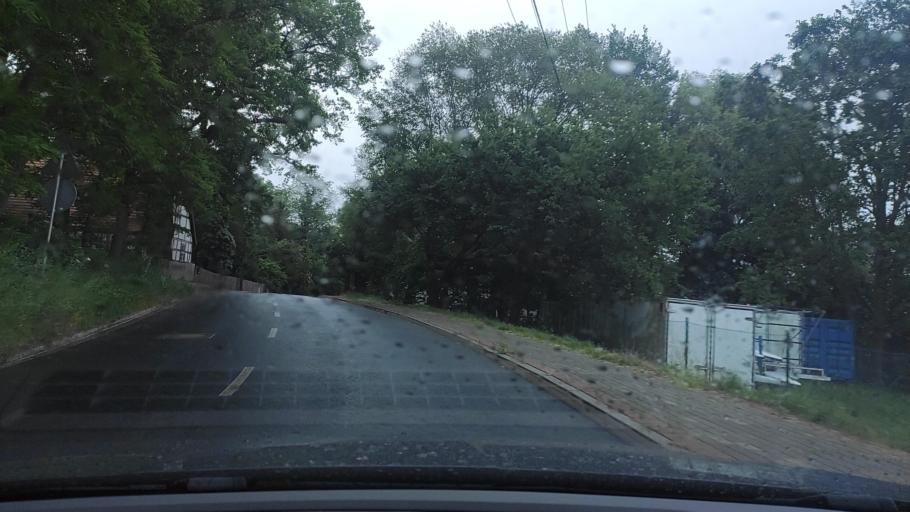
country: PL
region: Greater Poland Voivodeship
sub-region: Powiat poznanski
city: Kostrzyn
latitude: 52.4774
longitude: 17.1814
